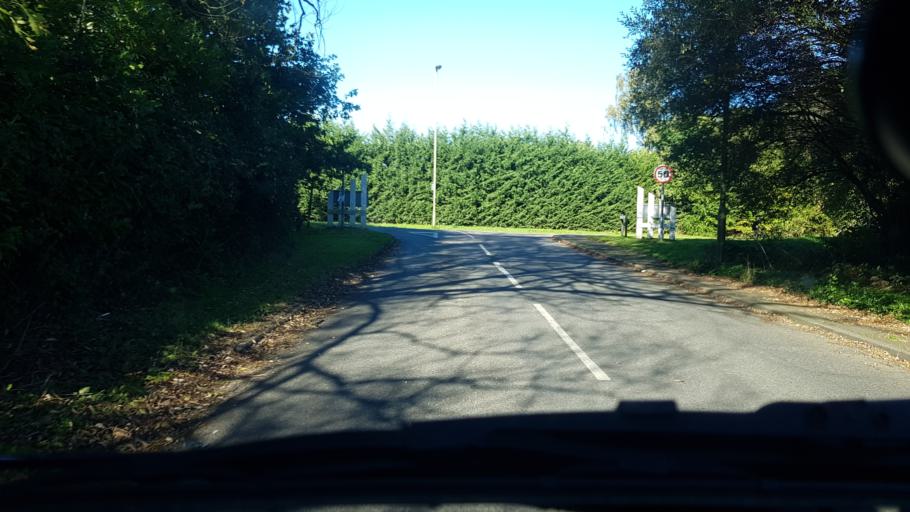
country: GB
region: England
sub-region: Surrey
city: Pirbright
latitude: 51.2643
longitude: -0.6392
